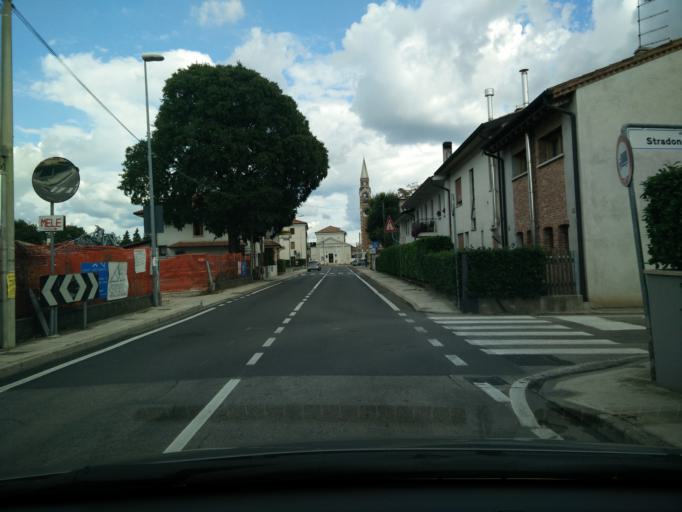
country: IT
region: Veneto
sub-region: Provincia di Treviso
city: Salvatronda
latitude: 45.6944
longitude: 11.9715
